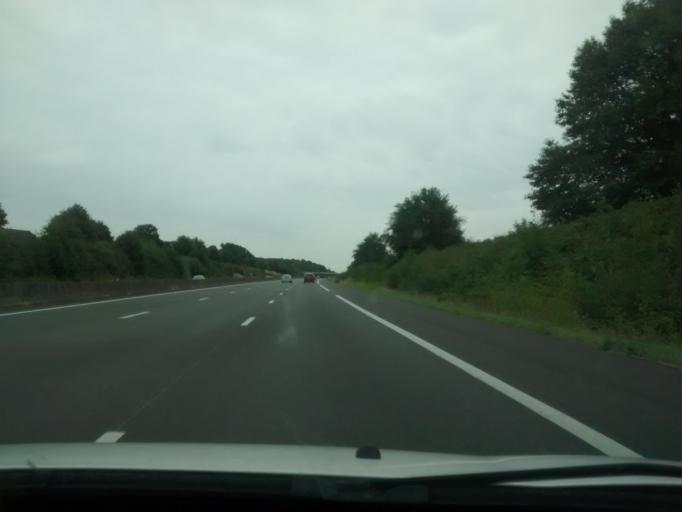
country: FR
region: Pays de la Loire
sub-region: Departement de la Sarthe
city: Connerre
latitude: 48.0824
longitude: 0.4923
